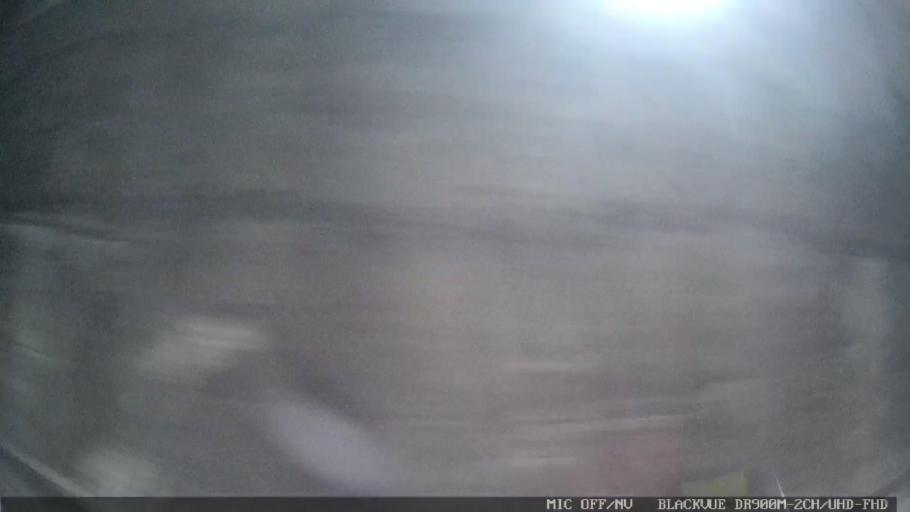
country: BR
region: Sao Paulo
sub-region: Cubatao
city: Cubatao
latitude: -23.8949
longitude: -46.4772
